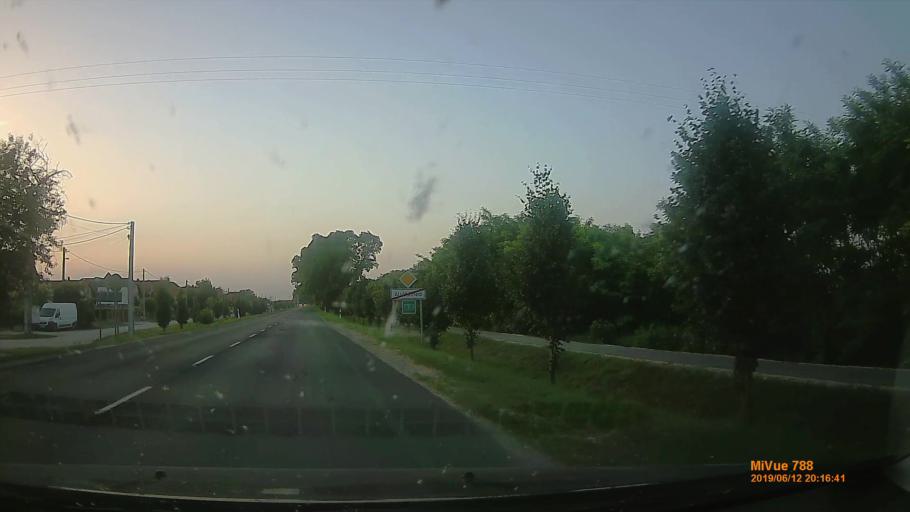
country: HU
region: Pest
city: Alsonemedi
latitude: 47.3211
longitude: 19.1631
